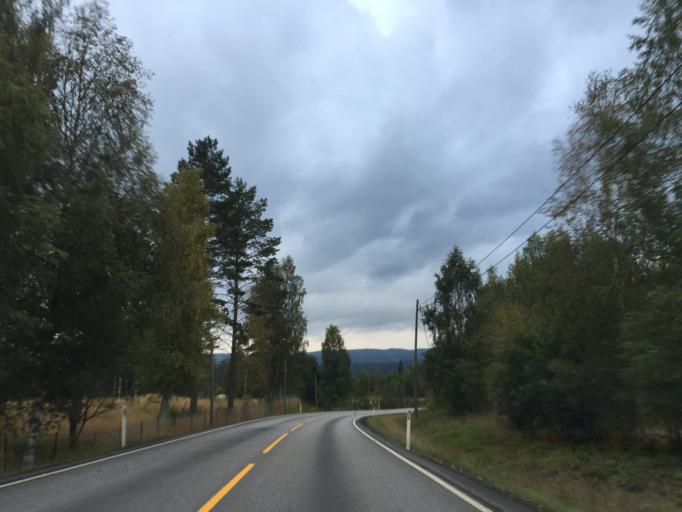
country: NO
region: Hedmark
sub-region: Nord-Odal
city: Sand
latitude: 60.4519
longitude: 11.5029
